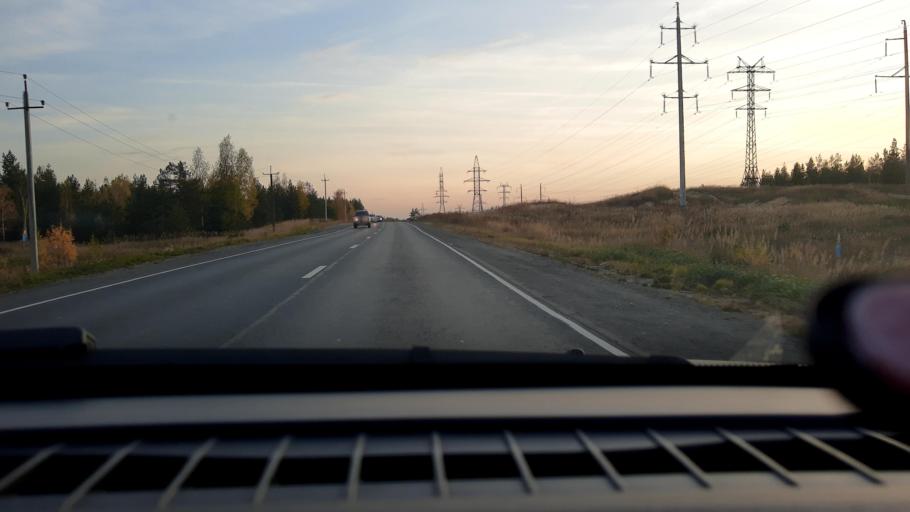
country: RU
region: Nizjnij Novgorod
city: Lukino
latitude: 56.3429
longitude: 43.5819
